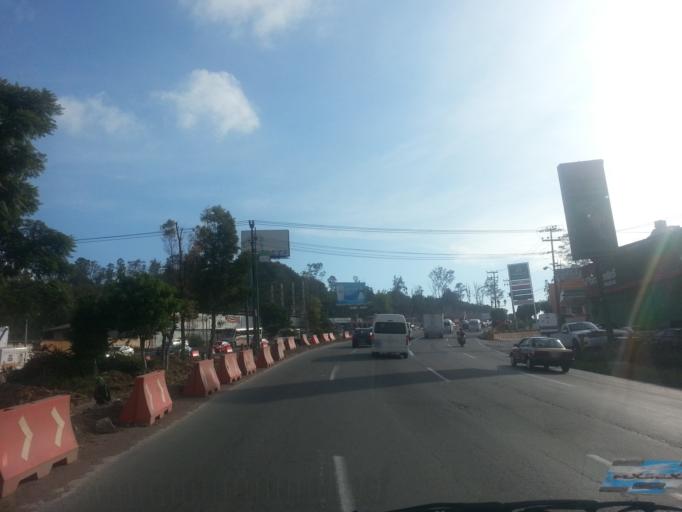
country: MX
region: Mexico City
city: Gustavo A. Madero
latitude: 19.5195
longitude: -99.0974
